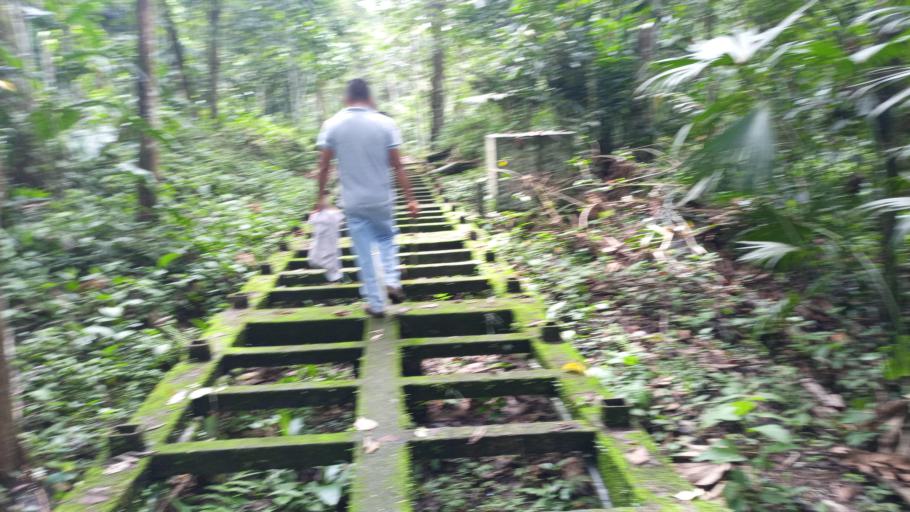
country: EC
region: Napo
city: Tena
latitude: -0.9960
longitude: -77.8171
